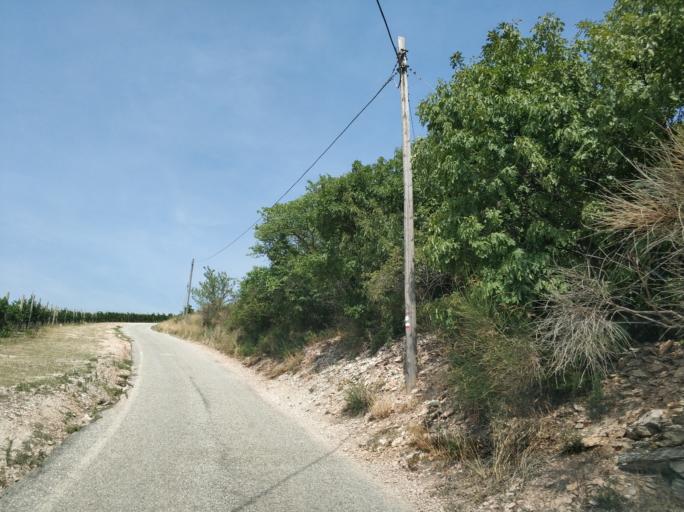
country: IT
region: Veneto
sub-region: Provincia di Padova
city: Arqua Petrarca
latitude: 45.2776
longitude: 11.7070
